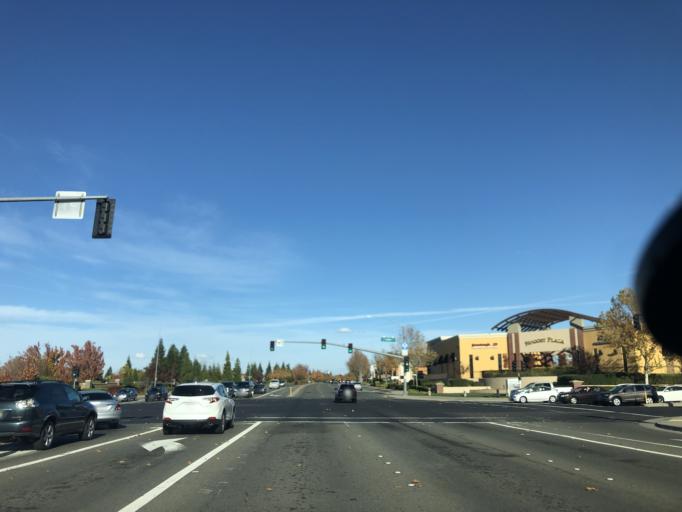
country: US
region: California
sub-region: Placer County
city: Roseville
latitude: 38.7891
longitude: -121.2820
